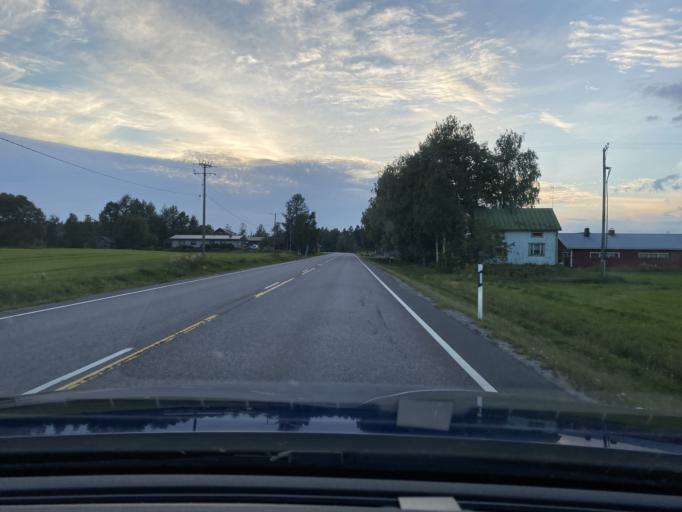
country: FI
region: Satakunta
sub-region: Pohjois-Satakunta
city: Kankaanpaeae
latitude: 61.7637
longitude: 22.4927
